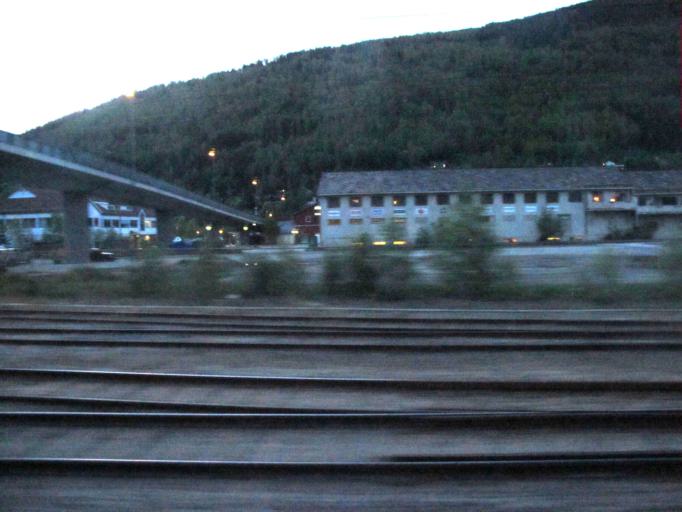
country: NO
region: Oppland
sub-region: Sel
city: Otta
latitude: 61.7713
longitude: 9.5377
